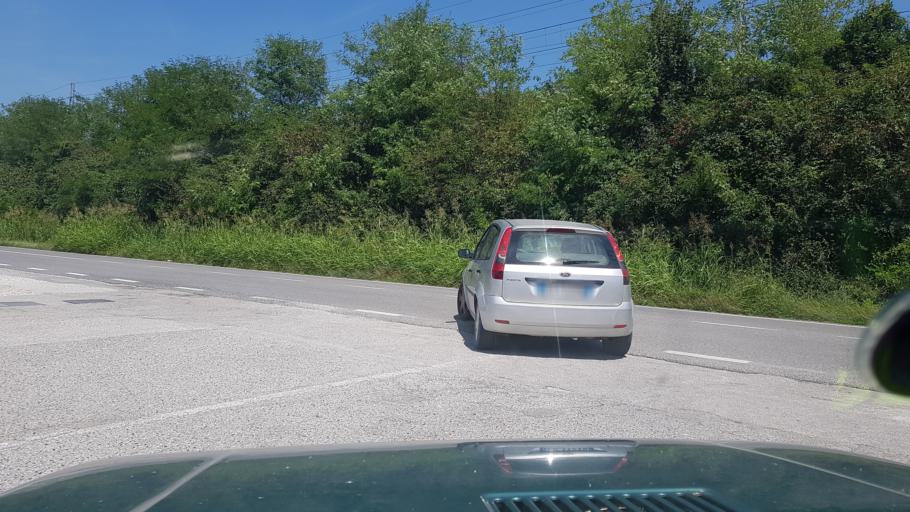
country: IT
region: Friuli Venezia Giulia
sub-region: Provincia di Gorizia
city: Cormons
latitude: 45.9496
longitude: 13.4766
